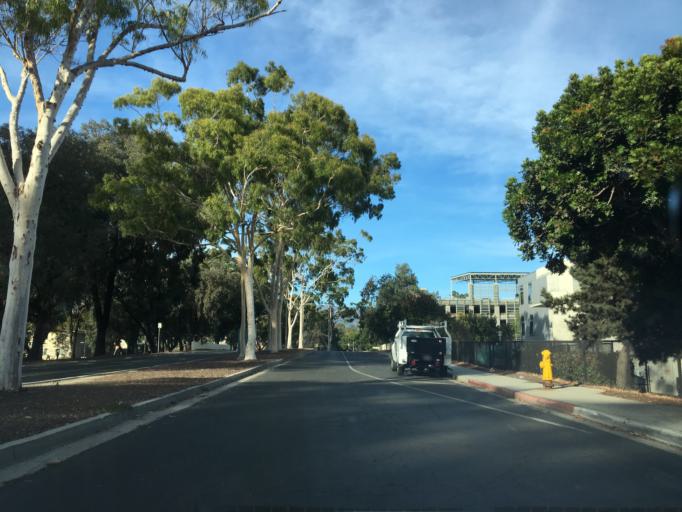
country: US
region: California
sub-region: Santa Barbara County
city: Isla Vista
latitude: 34.4122
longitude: -119.8532
